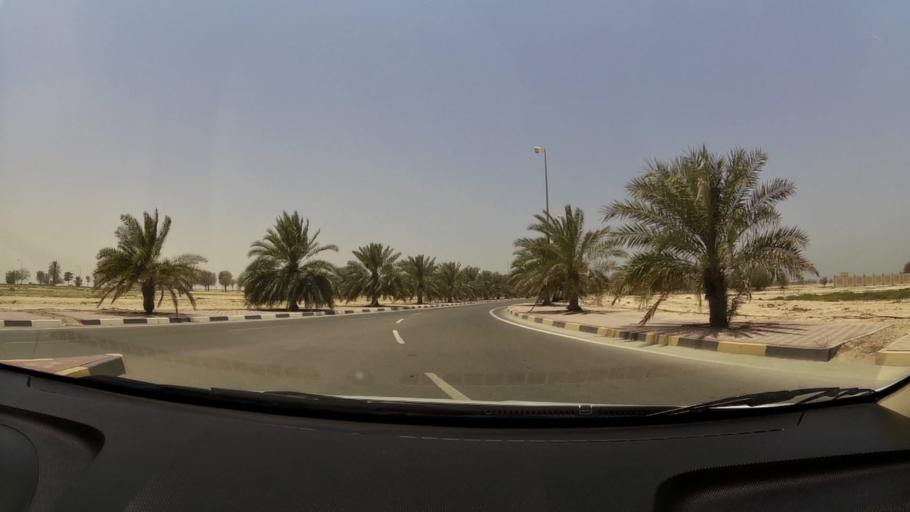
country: AE
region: Umm al Qaywayn
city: Umm al Qaywayn
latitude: 25.5300
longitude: 55.5374
